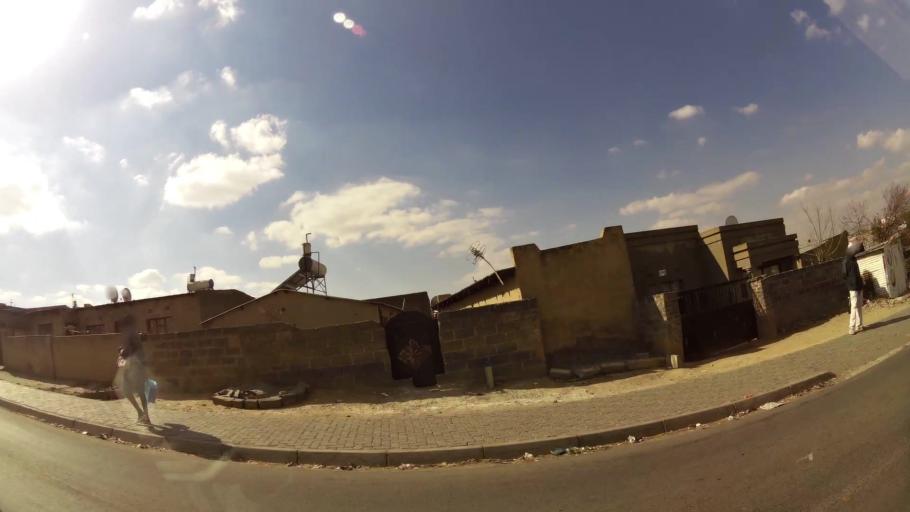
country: ZA
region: Gauteng
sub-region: Ekurhuleni Metropolitan Municipality
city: Tembisa
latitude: -26.0154
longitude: 28.1861
